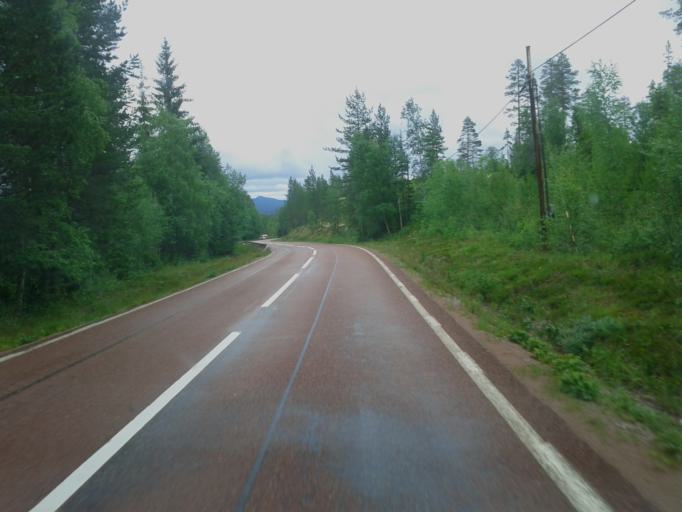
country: NO
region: Hedmark
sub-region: Trysil
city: Innbygda
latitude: 61.8524
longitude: 12.6392
